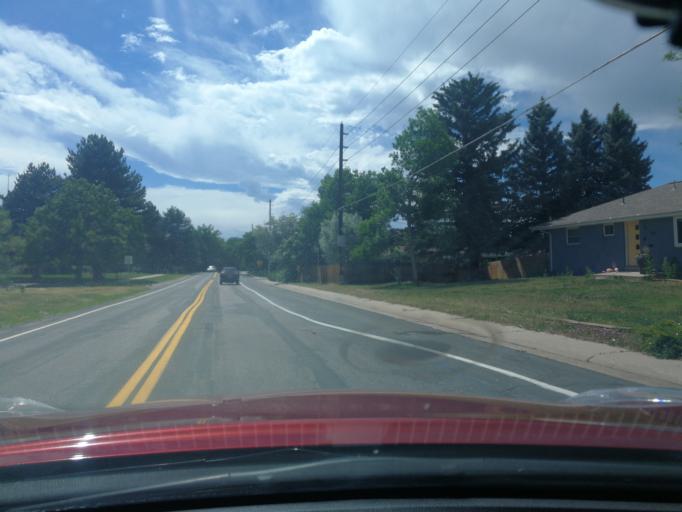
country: US
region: Colorado
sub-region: Arapahoe County
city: Littleton
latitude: 39.5915
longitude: -104.9978
